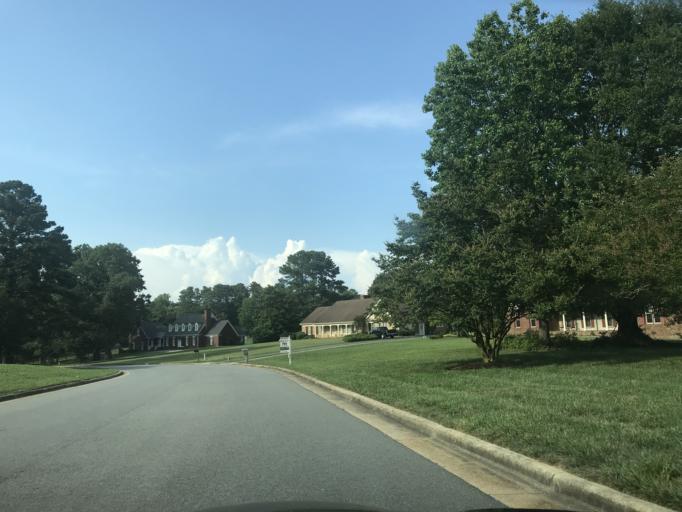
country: US
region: North Carolina
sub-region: Wake County
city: Knightdale
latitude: 35.8237
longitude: -78.5454
